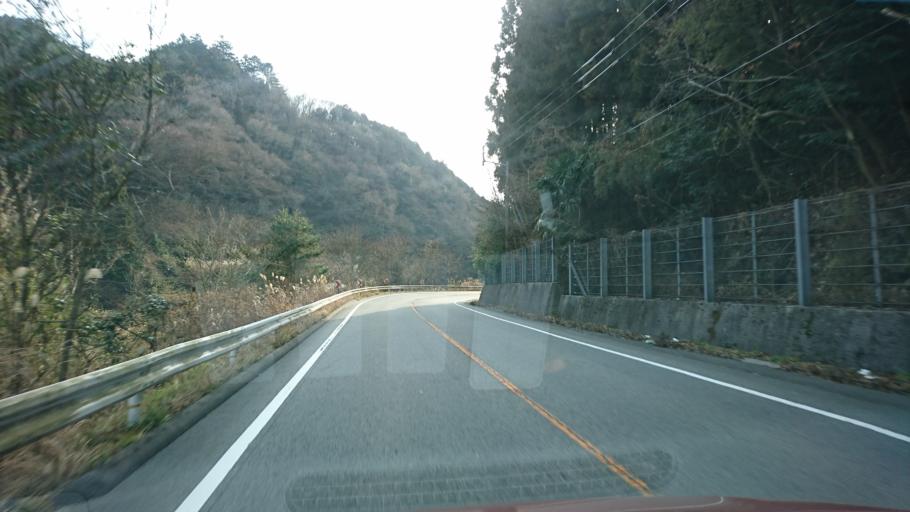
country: JP
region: Ehime
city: Hojo
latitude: 33.9288
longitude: 132.8946
